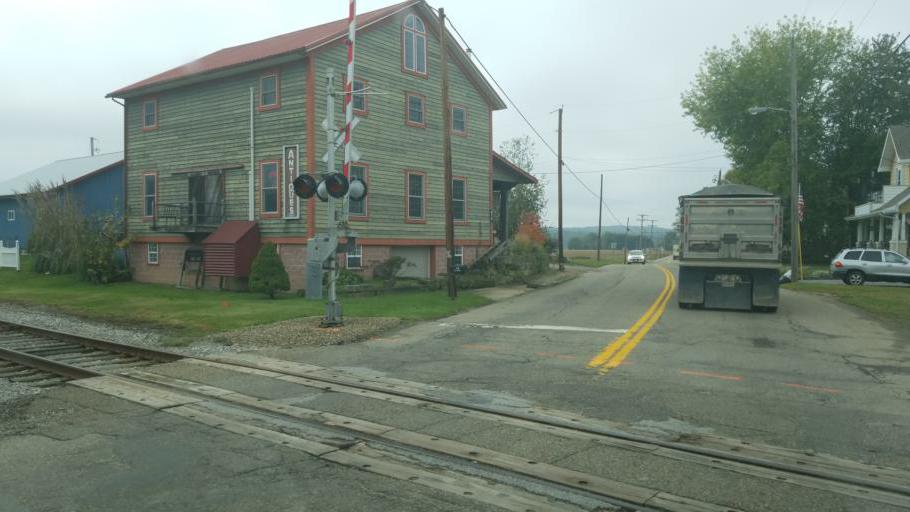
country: US
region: Ohio
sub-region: Stark County
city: Beach City
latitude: 40.6511
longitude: -81.5835
